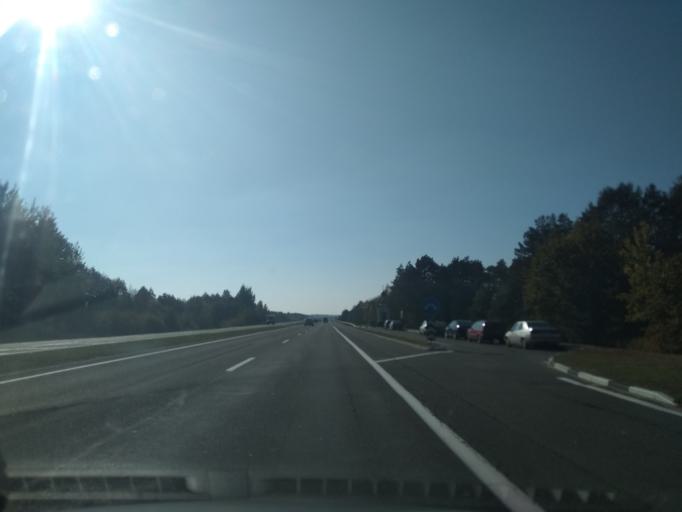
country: BY
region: Brest
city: Ivatsevichy
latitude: 52.7934
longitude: 25.5617
